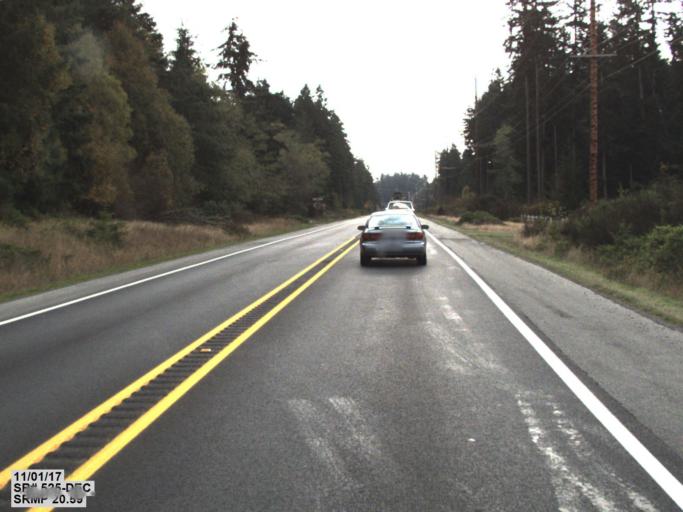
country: US
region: Washington
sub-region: Island County
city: Freeland
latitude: 48.0347
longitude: -122.5637
